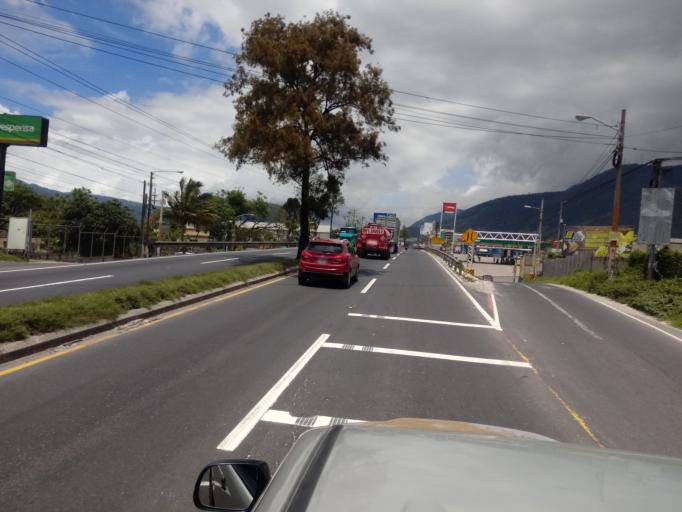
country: GT
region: Guatemala
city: Amatitlan
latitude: 14.4829
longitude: -90.6290
